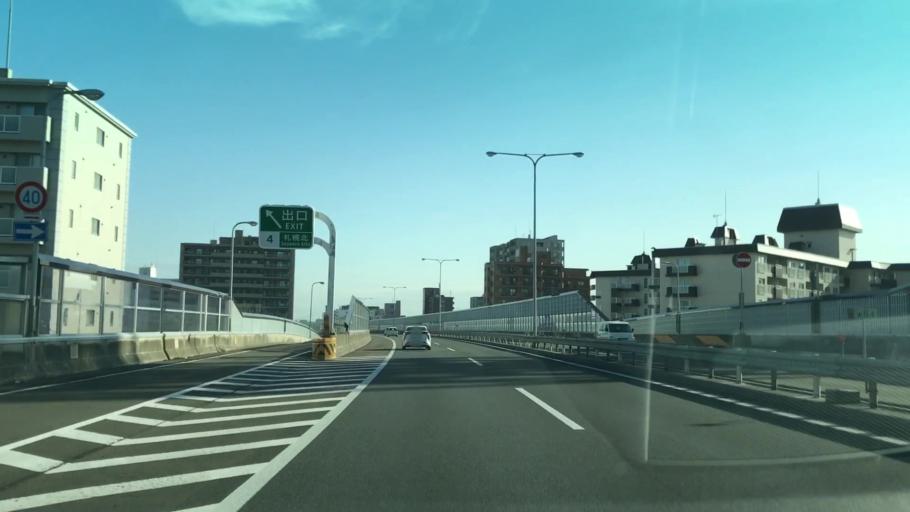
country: JP
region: Hokkaido
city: Sapporo
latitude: 43.1002
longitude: 141.3347
